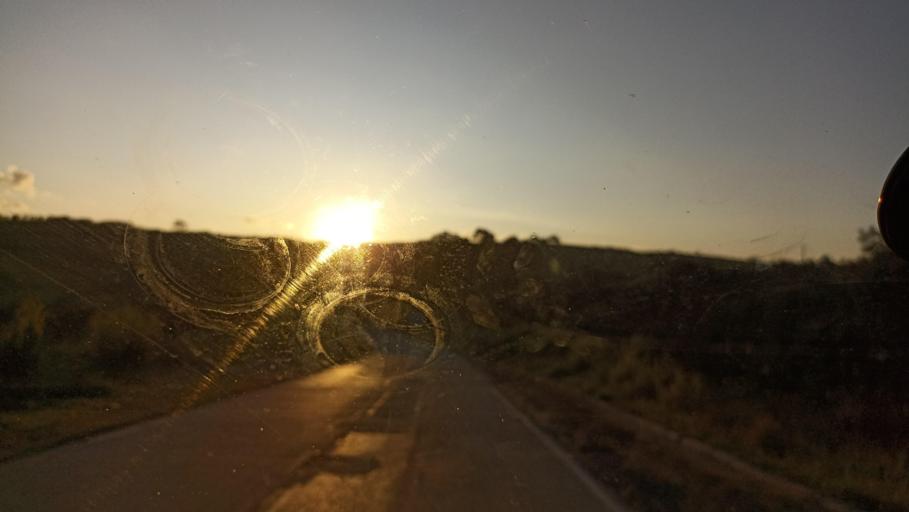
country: BR
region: Minas Gerais
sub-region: Sao Joao Del Rei
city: Sao Joao del Rei
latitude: -21.2296
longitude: -44.3812
